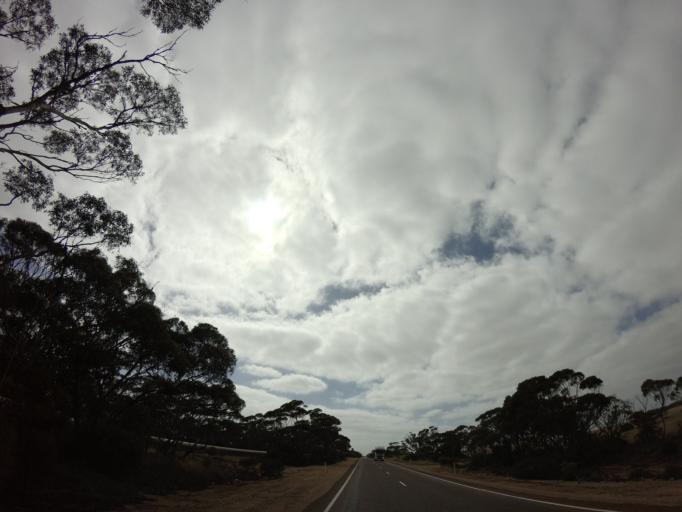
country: AU
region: South Australia
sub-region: Streaky Bay
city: Streaky Bay
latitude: -32.7278
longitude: 134.8695
